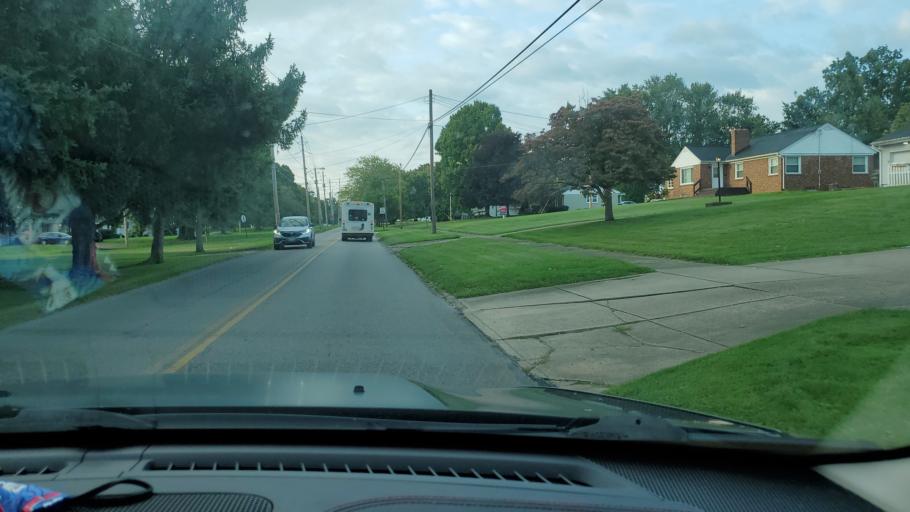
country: US
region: Ohio
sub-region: Mahoning County
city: Struthers
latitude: 41.0526
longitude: -80.6216
